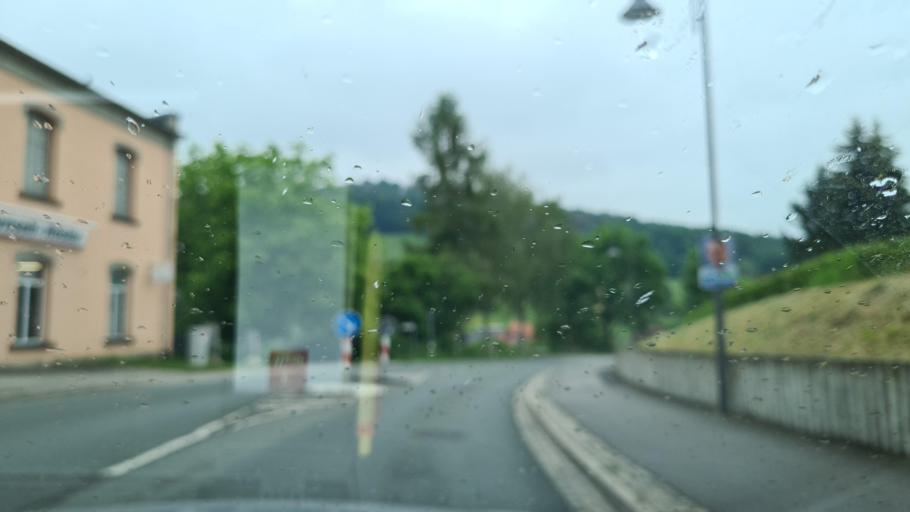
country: DE
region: Saxony
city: Schirgiswalde
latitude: 51.0793
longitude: 14.4328
